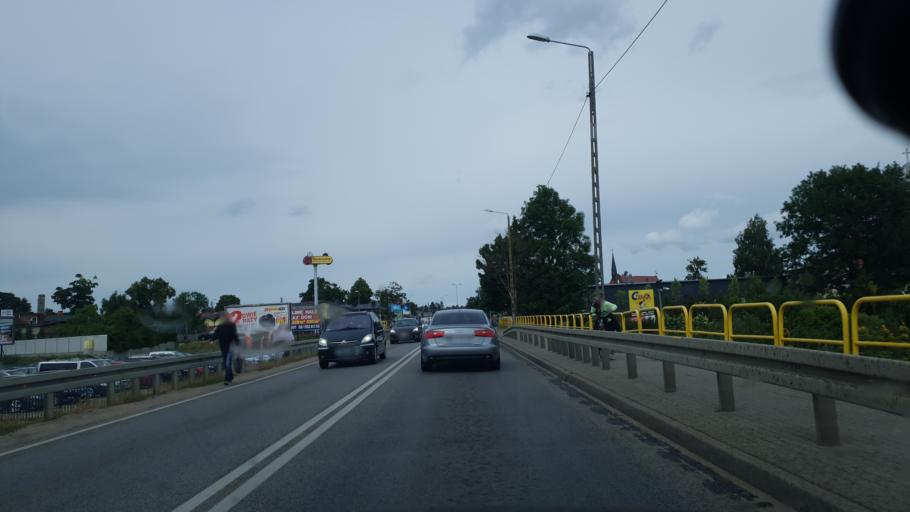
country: PL
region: Pomeranian Voivodeship
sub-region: Powiat kartuski
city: Chwaszczyno
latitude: 54.4418
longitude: 18.4167
